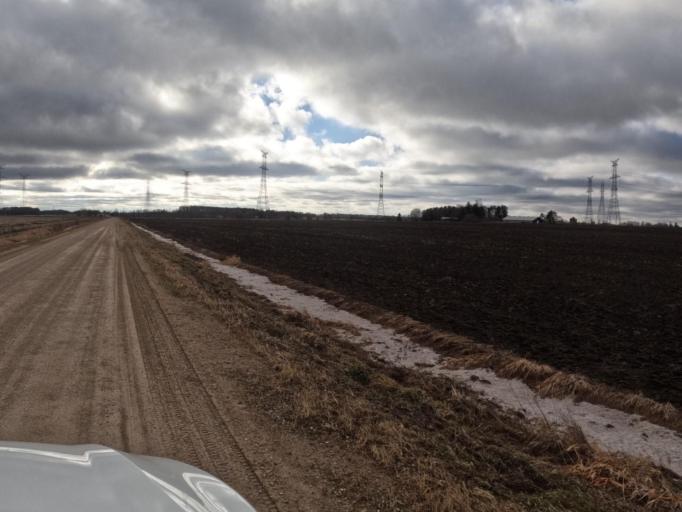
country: CA
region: Ontario
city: Shelburne
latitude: 43.9919
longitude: -80.3850
